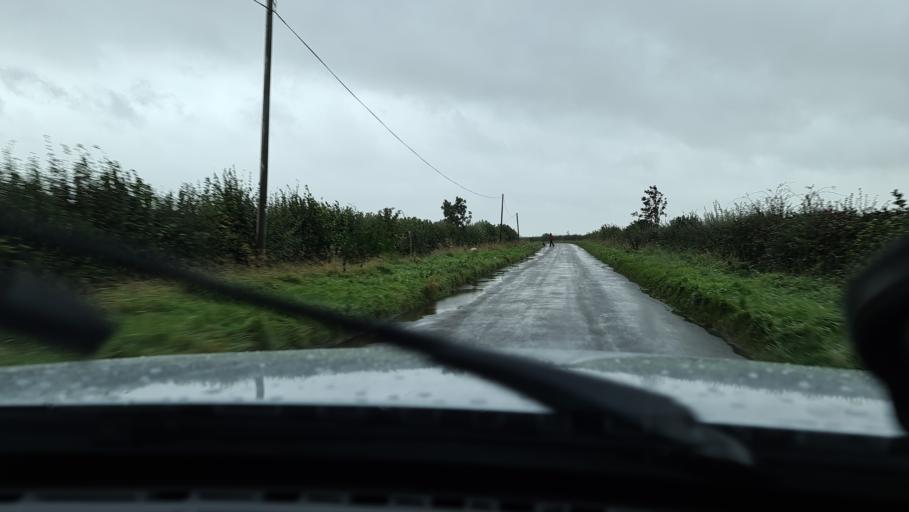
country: GB
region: England
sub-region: Oxfordshire
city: Woodstock
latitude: 51.9198
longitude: -1.3674
